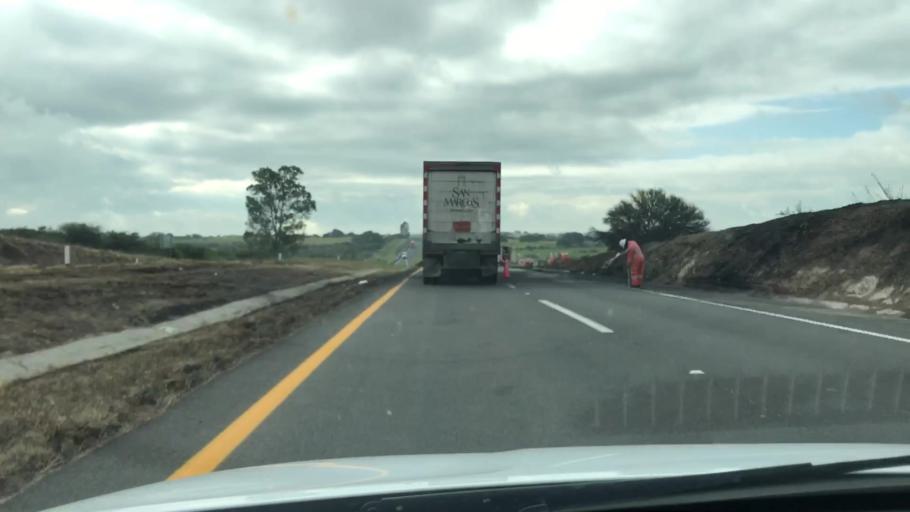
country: MX
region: Jalisco
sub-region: Union de San Antonio
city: San Jose del Caliche (El Caliche)
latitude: 21.2255
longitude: -101.9245
